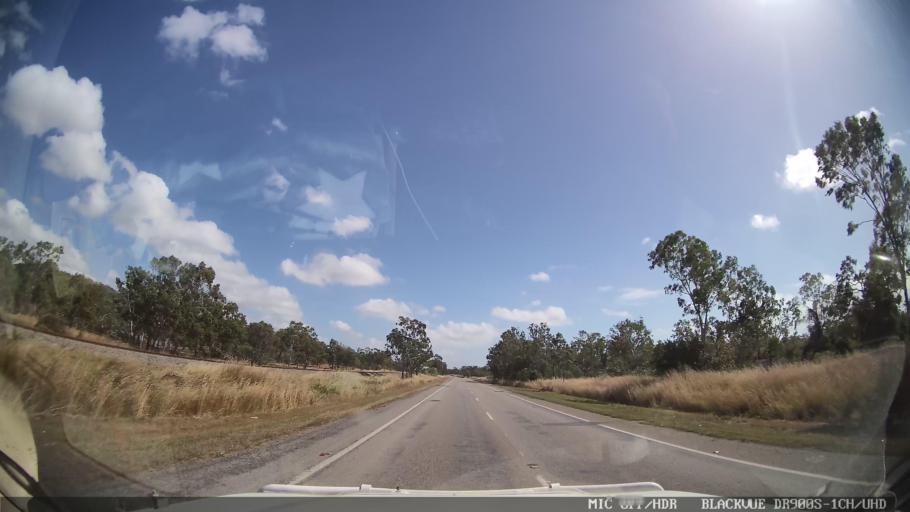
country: AU
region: Queensland
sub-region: Whitsunday
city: Bowen
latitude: -20.1802
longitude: 148.3501
